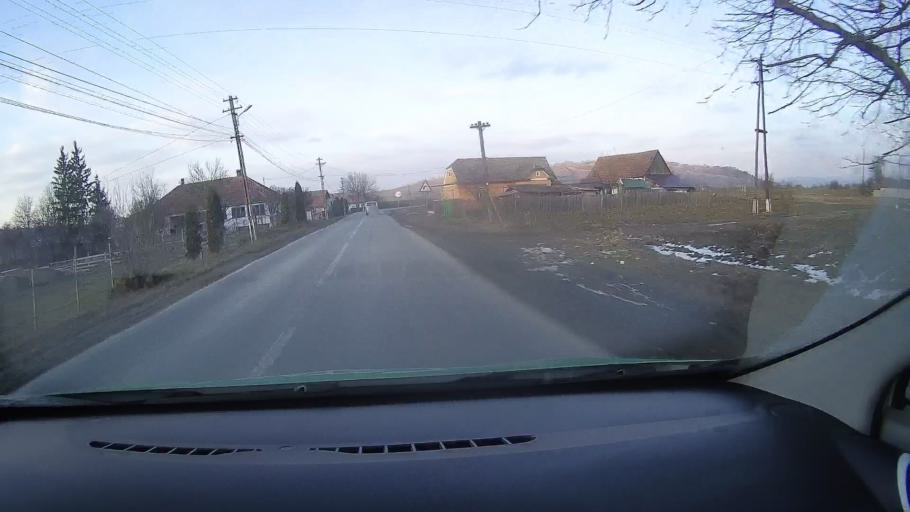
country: RO
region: Mures
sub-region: Comuna Vanatori
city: Vanatori
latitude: 46.2455
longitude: 24.9239
